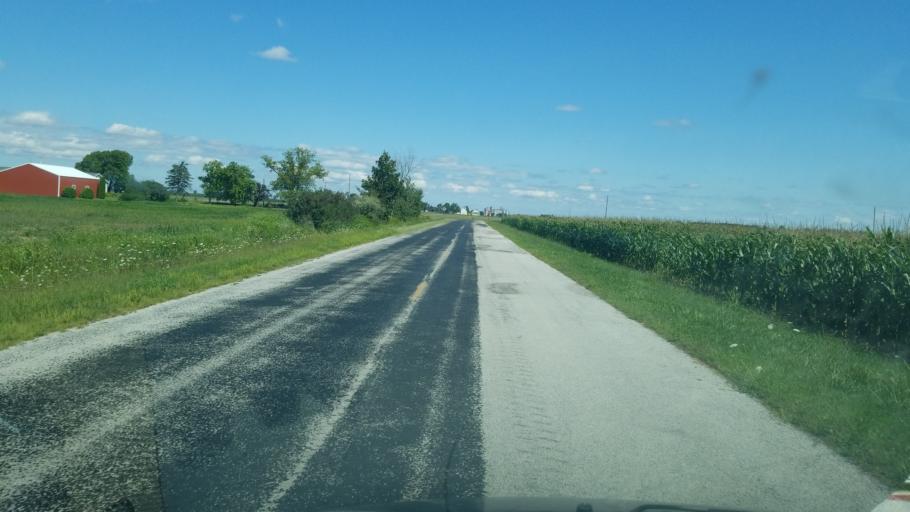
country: US
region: Ohio
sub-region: Henry County
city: Deshler
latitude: 41.2536
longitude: -83.8427
